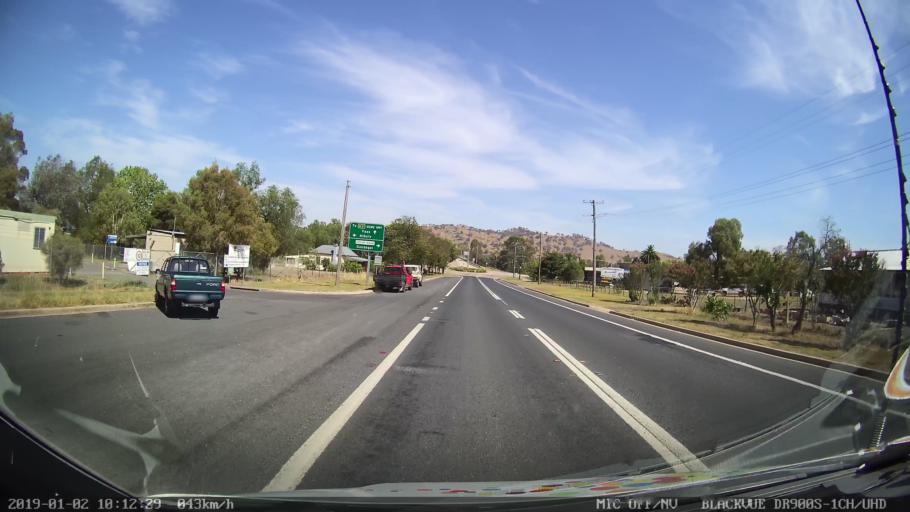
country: AU
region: New South Wales
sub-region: Gundagai
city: Gundagai
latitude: -35.0848
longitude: 148.0952
